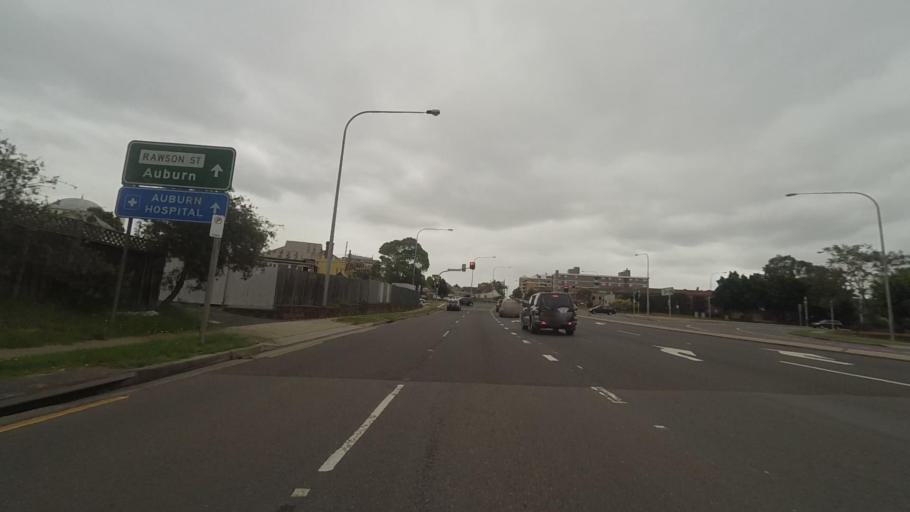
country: AU
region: New South Wales
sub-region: Auburn
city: Auburn
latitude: -33.8519
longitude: 151.0378
